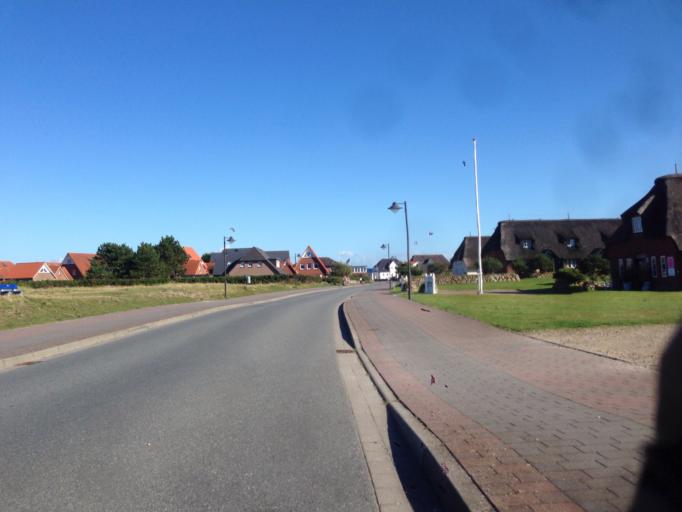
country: DE
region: Schleswig-Holstein
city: List
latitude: 55.0212
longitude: 8.4315
